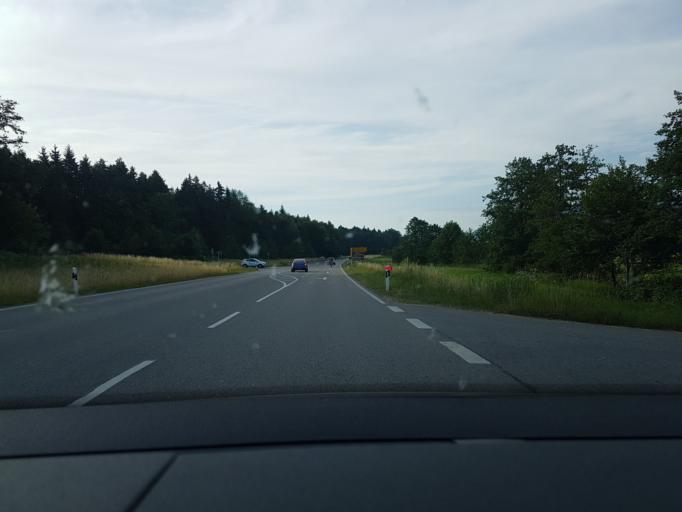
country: DE
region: Bavaria
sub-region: Upper Bavaria
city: Ainring
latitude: 47.8573
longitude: 12.9347
